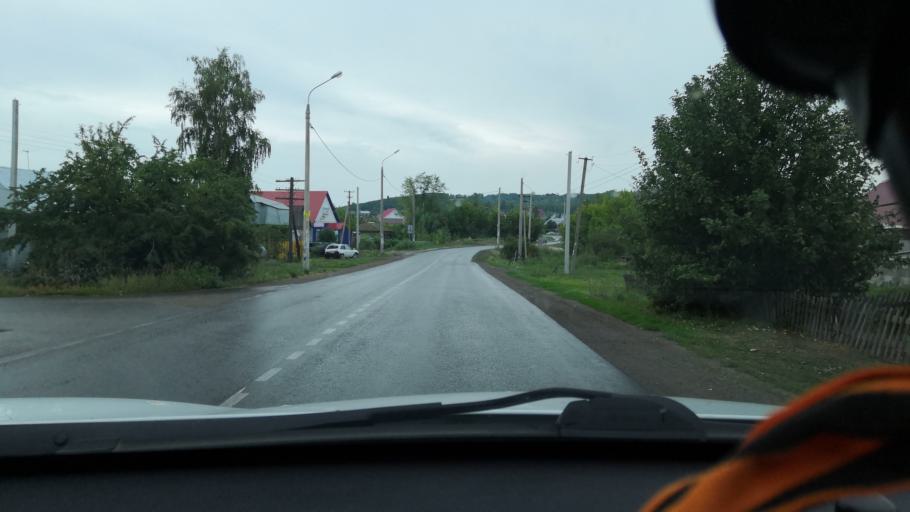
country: RU
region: Samara
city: Novosemeykino
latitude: 53.3772
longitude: 50.3485
